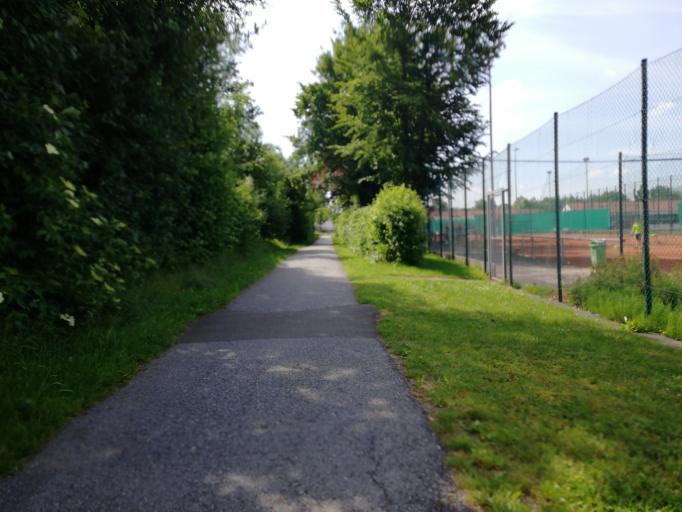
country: DE
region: North Rhine-Westphalia
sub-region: Regierungsbezirk Detmold
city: Verl
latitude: 51.8925
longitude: 8.4635
